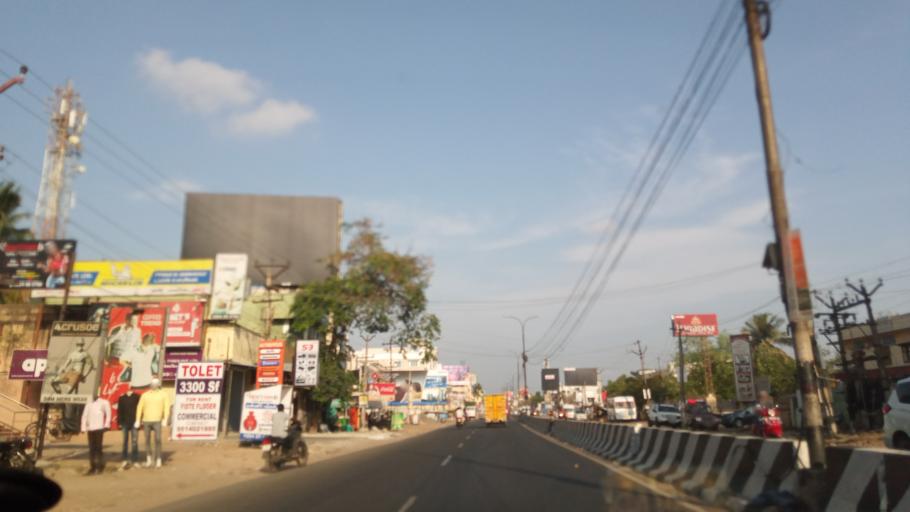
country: IN
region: Tamil Nadu
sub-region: Kancheepuram
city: Poonamalle
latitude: 13.0428
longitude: 80.1234
